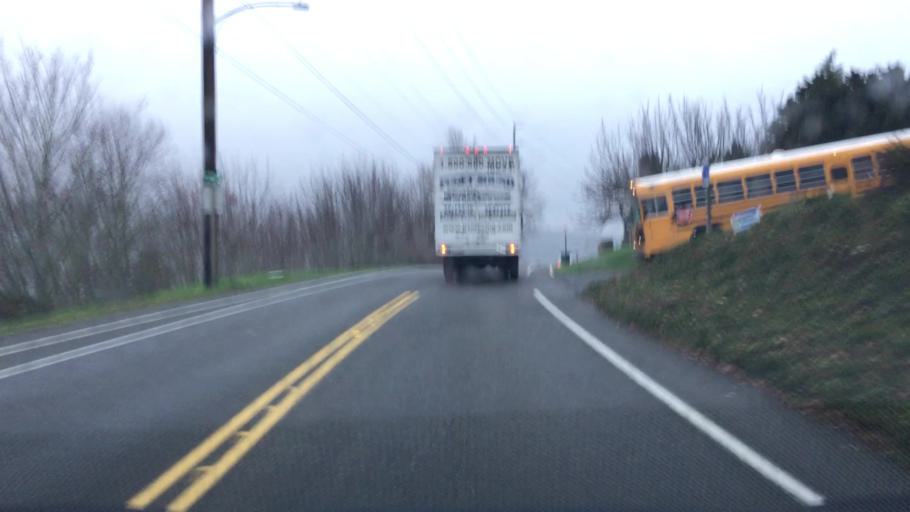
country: US
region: Washington
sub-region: King County
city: Renton
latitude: 47.5182
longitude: -122.2093
